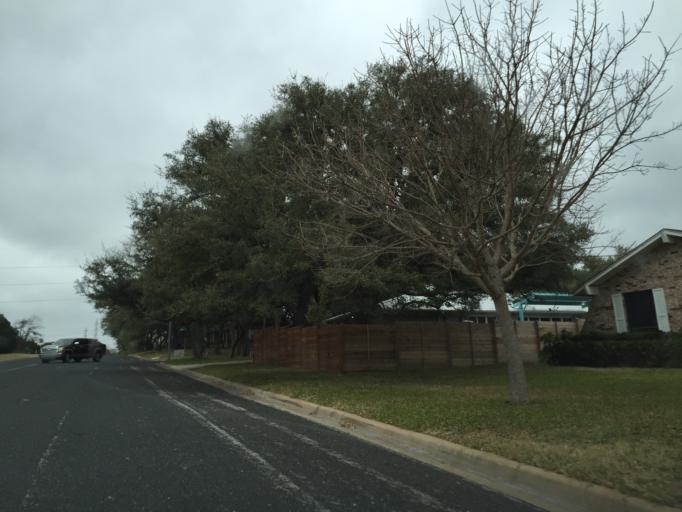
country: US
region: Texas
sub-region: Travis County
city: Wells Branch
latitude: 30.4054
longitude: -97.6841
